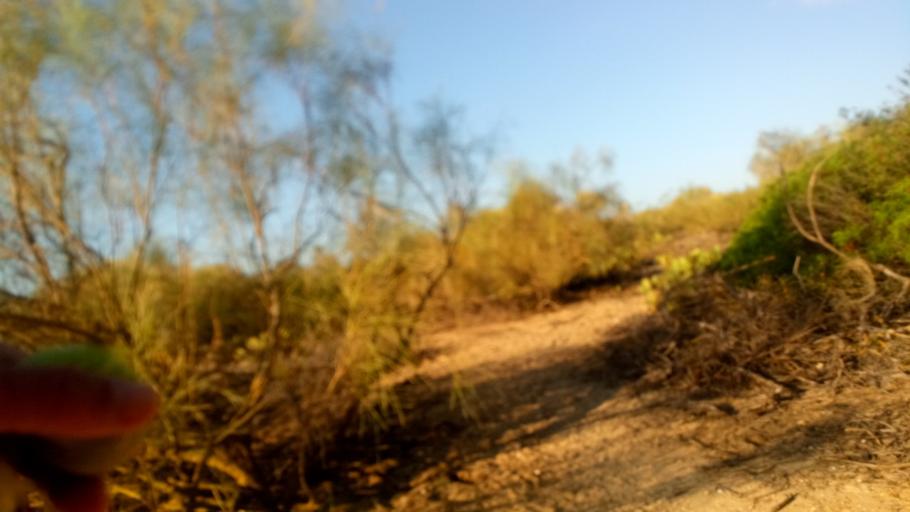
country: PT
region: Faro
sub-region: Tavira
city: Tavira
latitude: 37.1427
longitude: -7.5824
